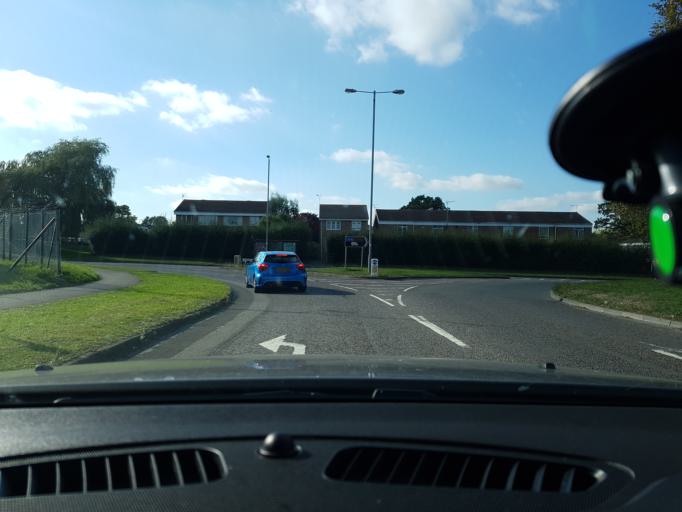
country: GB
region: England
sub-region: Borough of Swindon
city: Wanborough
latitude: 51.5535
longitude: -1.7266
